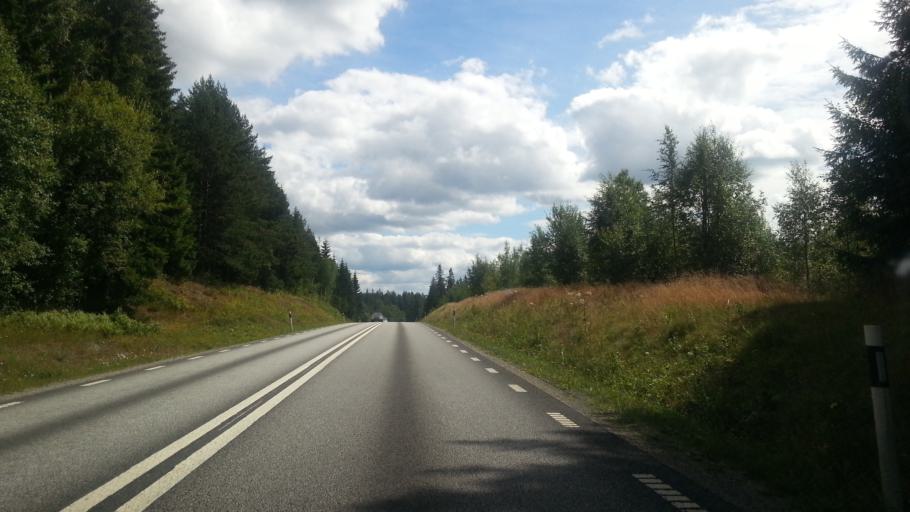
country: SE
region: OErebro
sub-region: Lindesbergs Kommun
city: Stora
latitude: 59.6489
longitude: 15.1195
